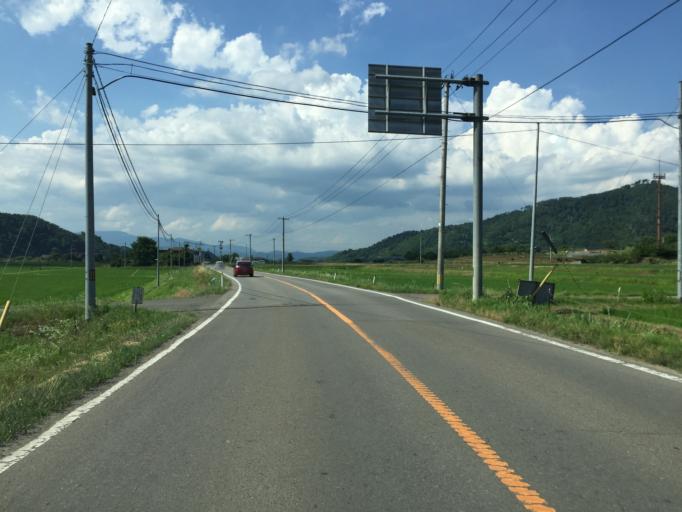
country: JP
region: Fukushima
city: Yanagawamachi-saiwaicho
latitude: 37.8062
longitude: 140.6199
